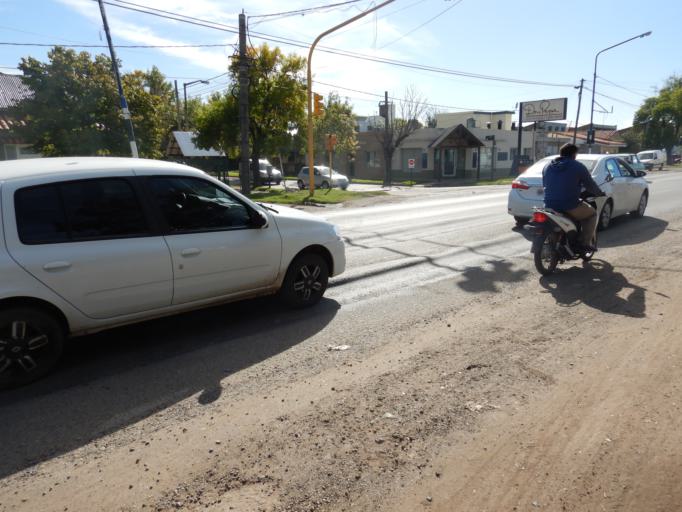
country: AR
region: Santa Fe
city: Roldan
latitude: -32.9056
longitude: -60.9090
